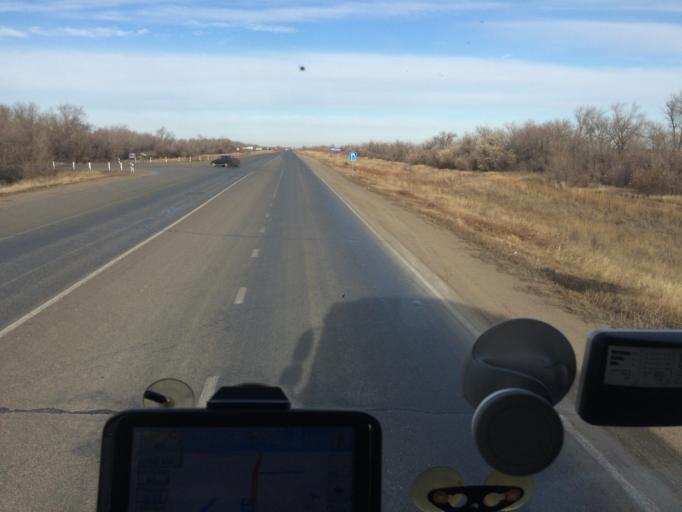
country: KZ
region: Batys Qazaqstan
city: Oral
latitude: 51.3111
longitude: 51.3513
